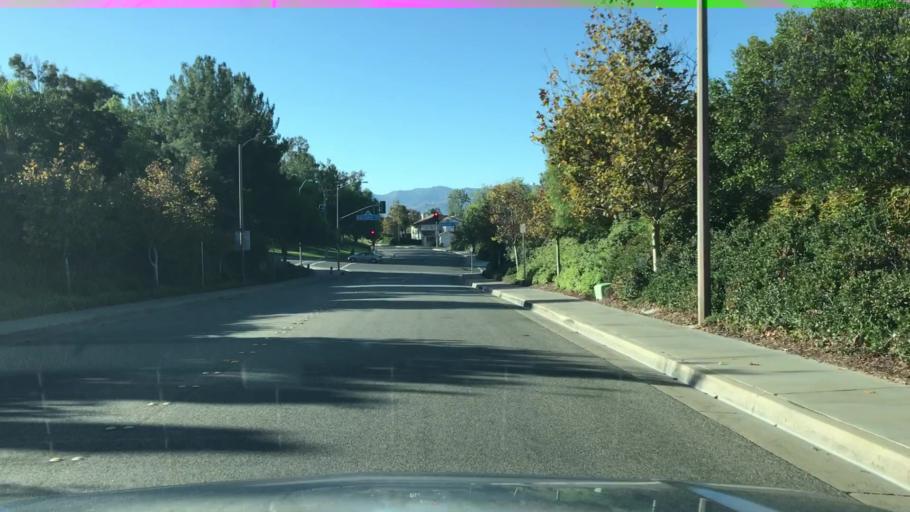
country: US
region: California
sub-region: Los Angeles County
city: Santa Clarita
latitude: 34.4439
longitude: -118.5492
